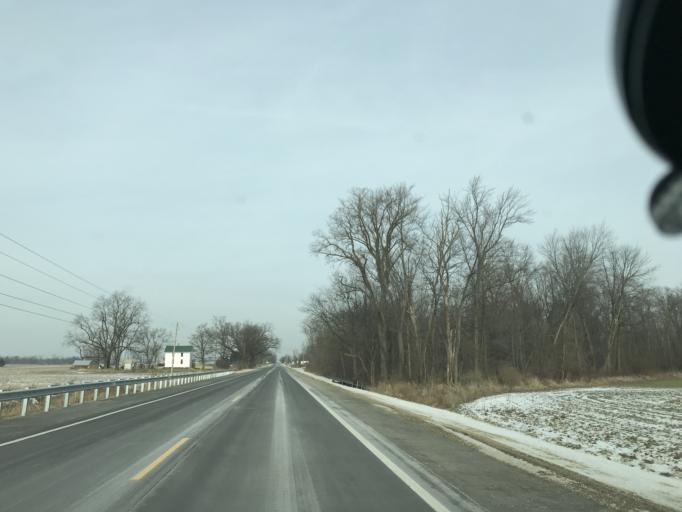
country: US
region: Michigan
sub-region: Ionia County
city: Lake Odessa
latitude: 42.8511
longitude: -85.0749
